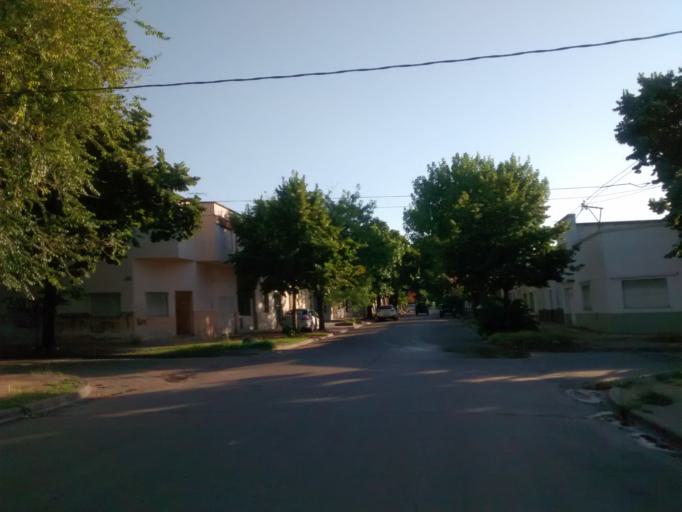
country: AR
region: Buenos Aires
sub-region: Partido de La Plata
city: La Plata
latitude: -34.9167
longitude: -57.9287
